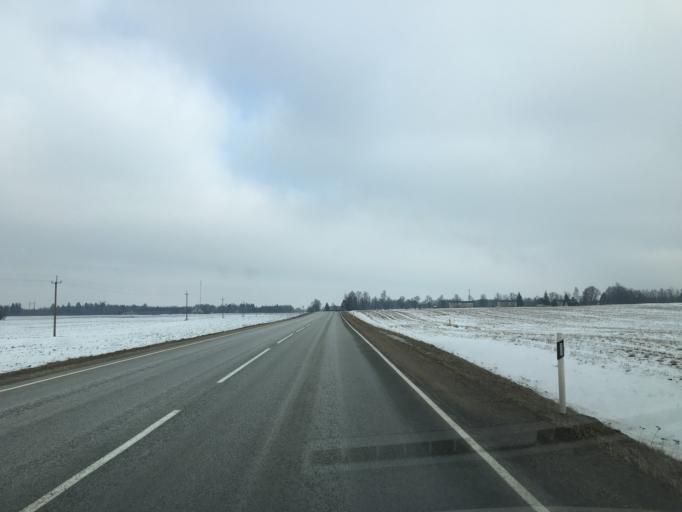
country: EE
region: Tartu
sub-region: Elva linn
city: Elva
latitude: 58.1191
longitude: 26.2402
